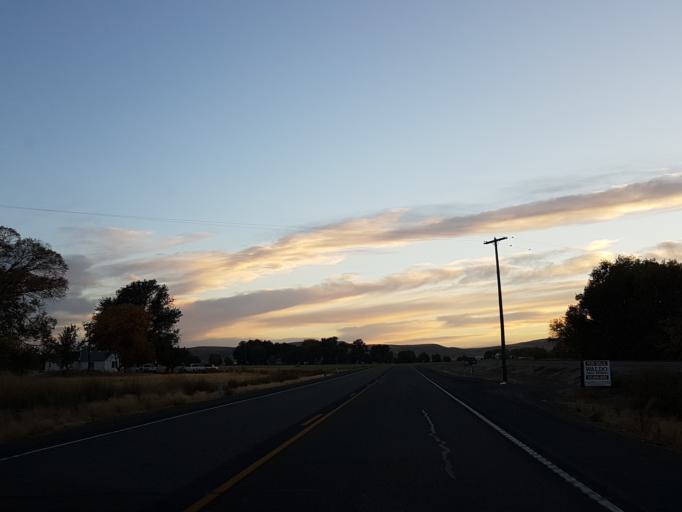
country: US
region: Oregon
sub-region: Malheur County
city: Vale
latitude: 43.9393
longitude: -117.3085
